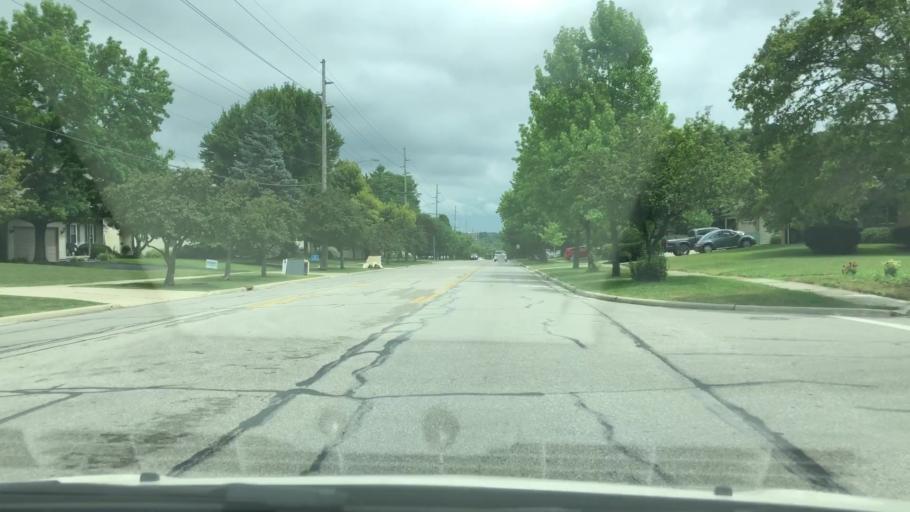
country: US
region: Ohio
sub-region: Franklin County
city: Westerville
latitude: 40.1250
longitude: -82.9559
